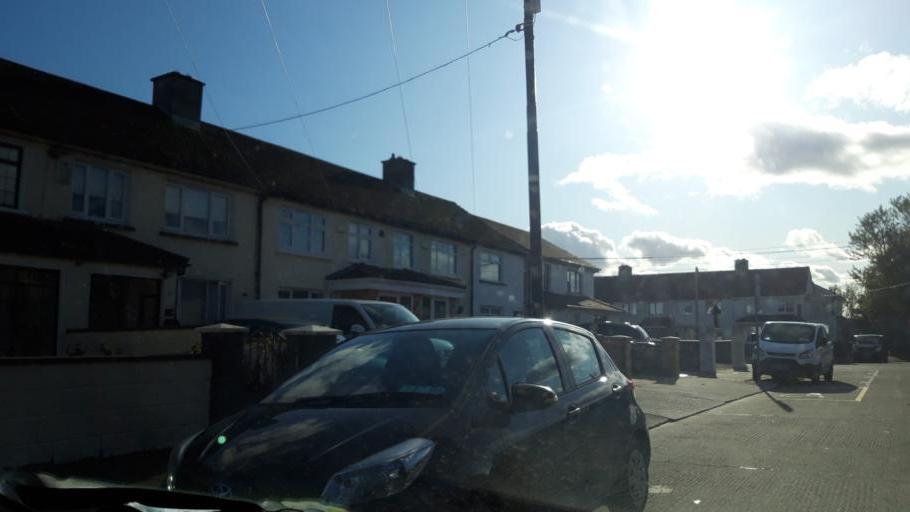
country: IE
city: Coolock
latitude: 53.3859
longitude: -6.1956
